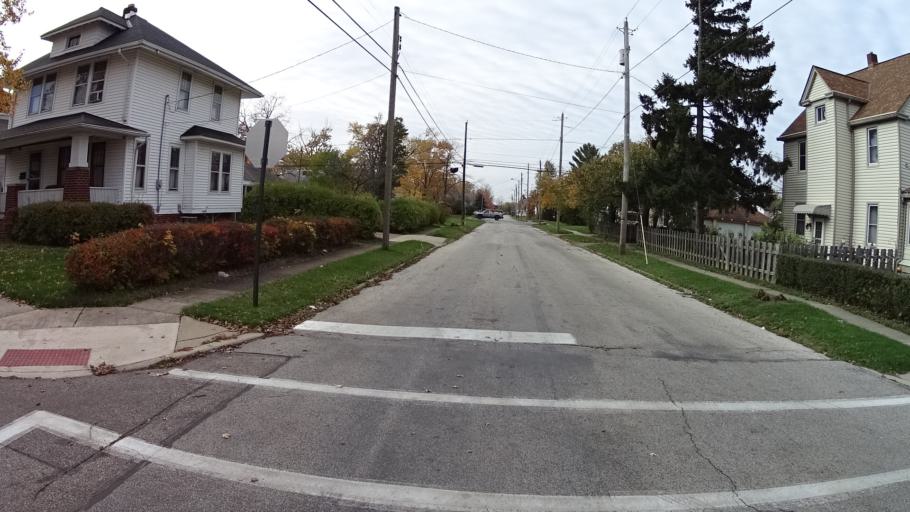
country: US
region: Ohio
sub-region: Lorain County
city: Lorain
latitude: 41.4710
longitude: -82.1629
